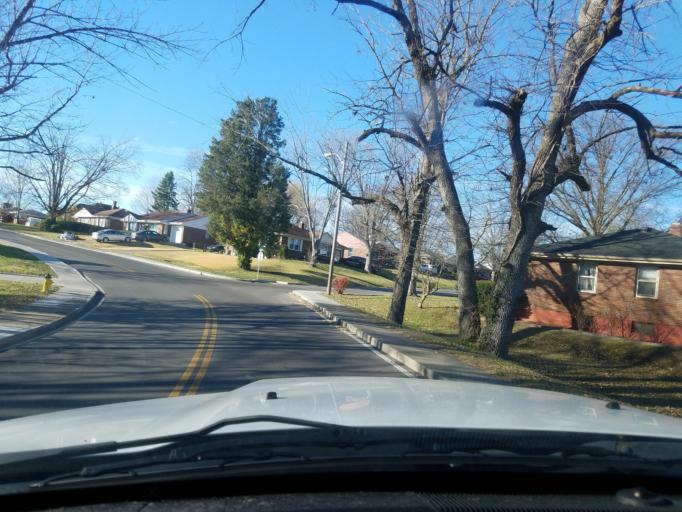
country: US
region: Indiana
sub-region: Floyd County
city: New Albany
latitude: 38.3039
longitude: -85.8332
